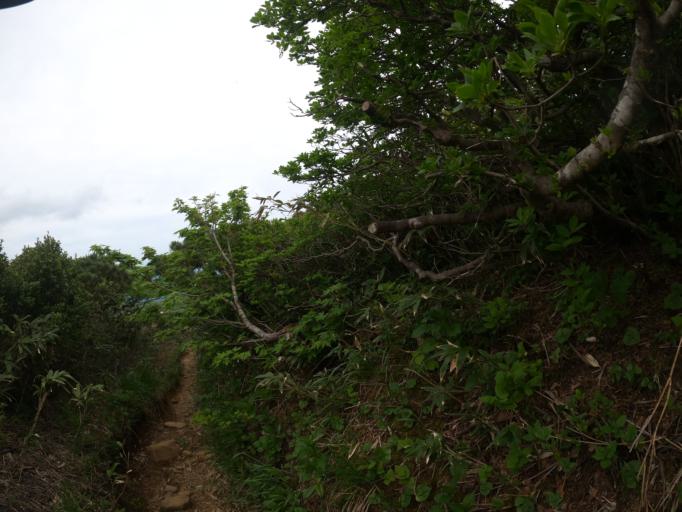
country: JP
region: Iwate
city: Ichinoseki
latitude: 38.9613
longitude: 140.7885
